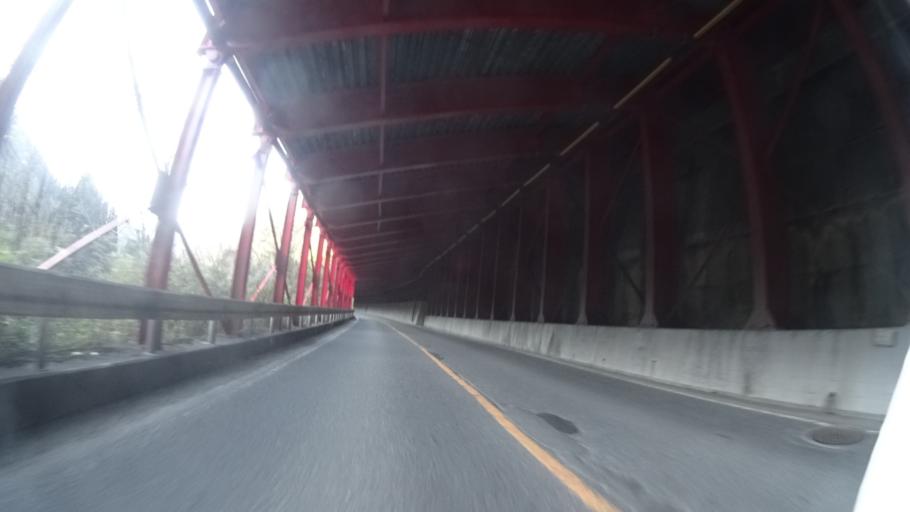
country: JP
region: Fukui
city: Ono
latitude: 35.9053
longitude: 136.6471
